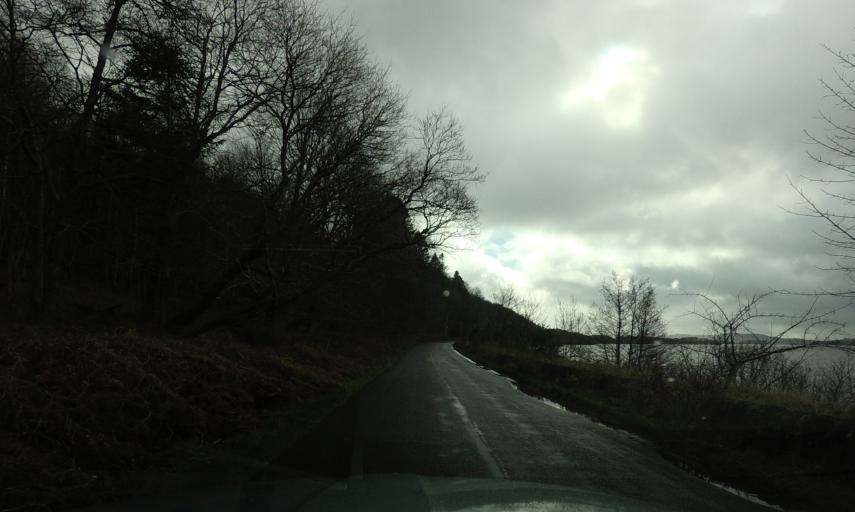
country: GB
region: Scotland
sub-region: West Dunbartonshire
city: Balloch
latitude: 56.1181
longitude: -4.5885
